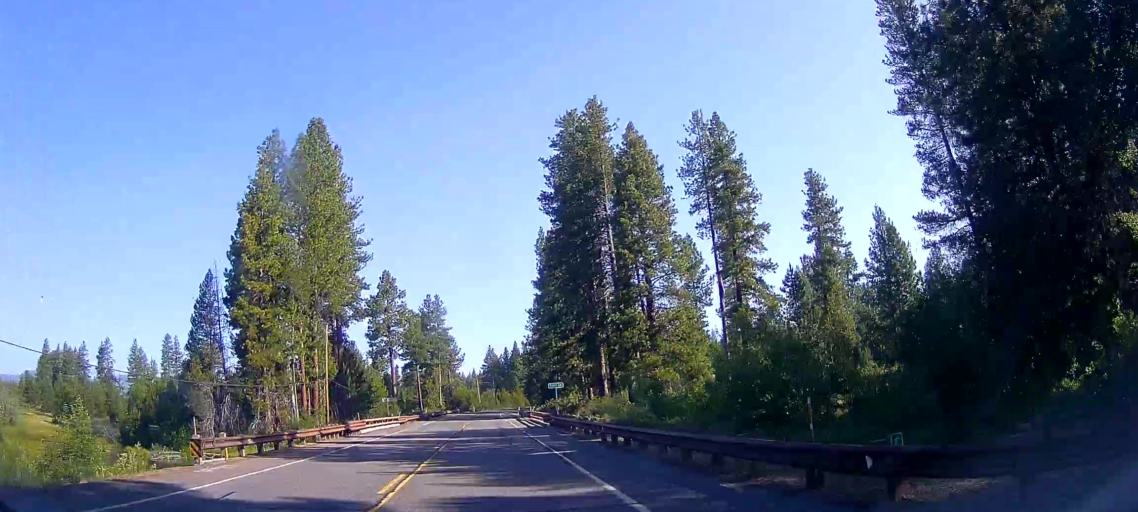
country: US
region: Oregon
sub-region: Klamath County
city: Klamath Falls
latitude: 42.6811
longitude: -121.9728
